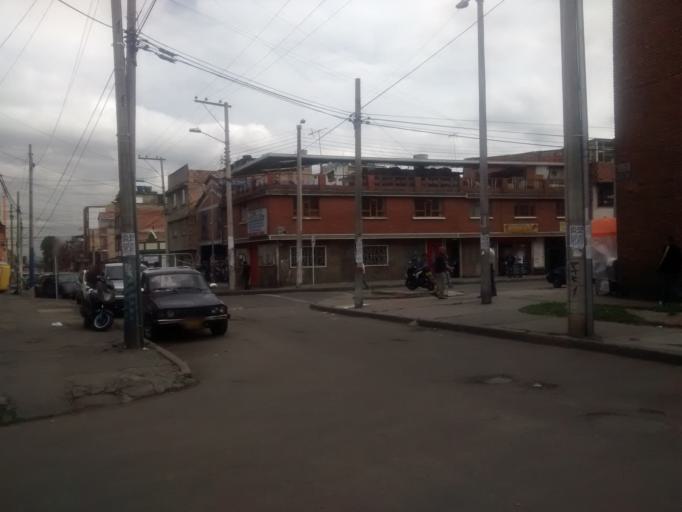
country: CO
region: Bogota D.C.
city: Bogota
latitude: 4.5860
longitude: -74.1051
